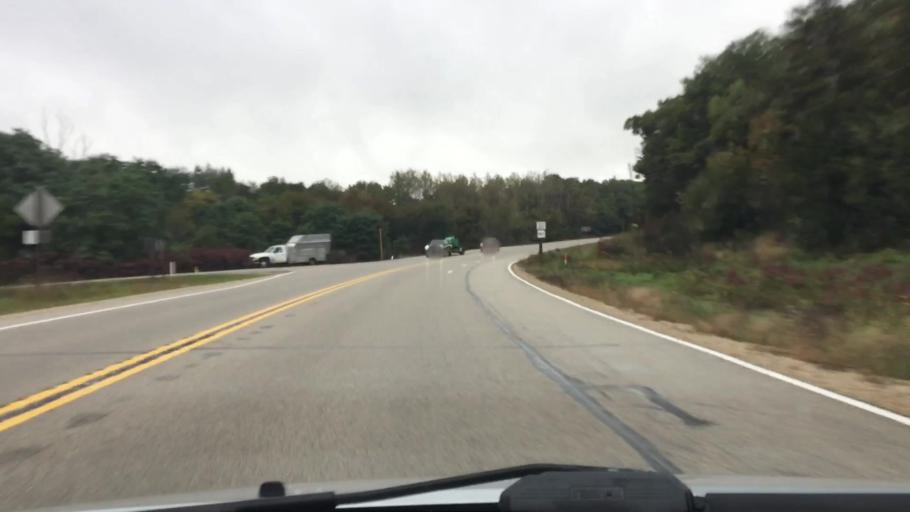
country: US
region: Wisconsin
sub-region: Waukesha County
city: Eagle
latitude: 42.9381
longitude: -88.4714
